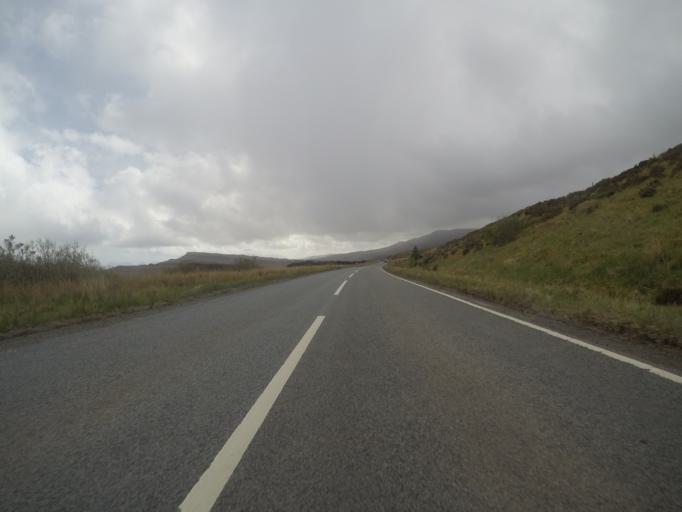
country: GB
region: Scotland
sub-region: Highland
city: Portree
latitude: 57.5029
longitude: -6.1535
